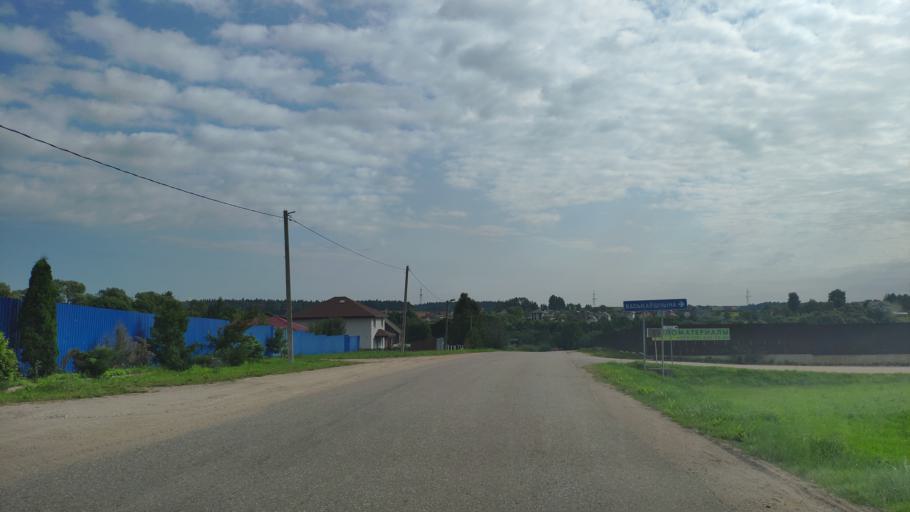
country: BY
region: Minsk
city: Khatsyezhyna
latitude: 53.8631
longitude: 27.3135
